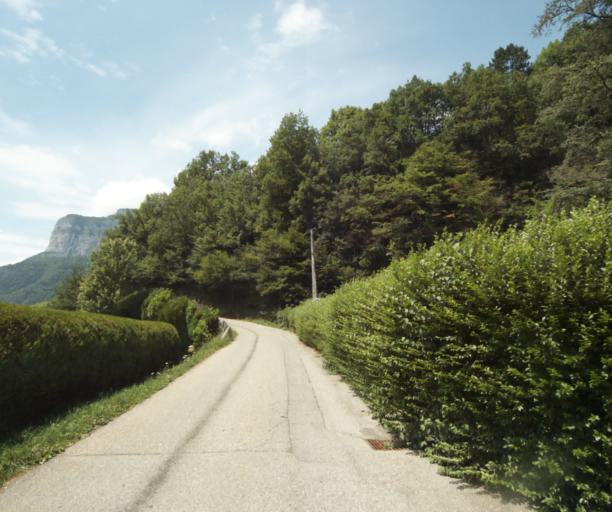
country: FR
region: Rhone-Alpes
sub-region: Departement de la Haute-Savoie
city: Thones
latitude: 45.8987
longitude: 6.3018
